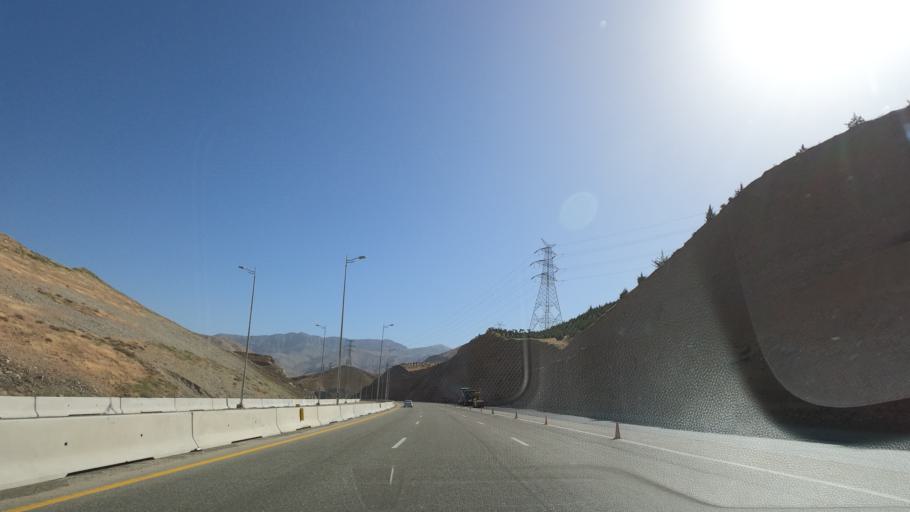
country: IR
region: Alborz
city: Karaj
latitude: 35.8130
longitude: 51.0367
